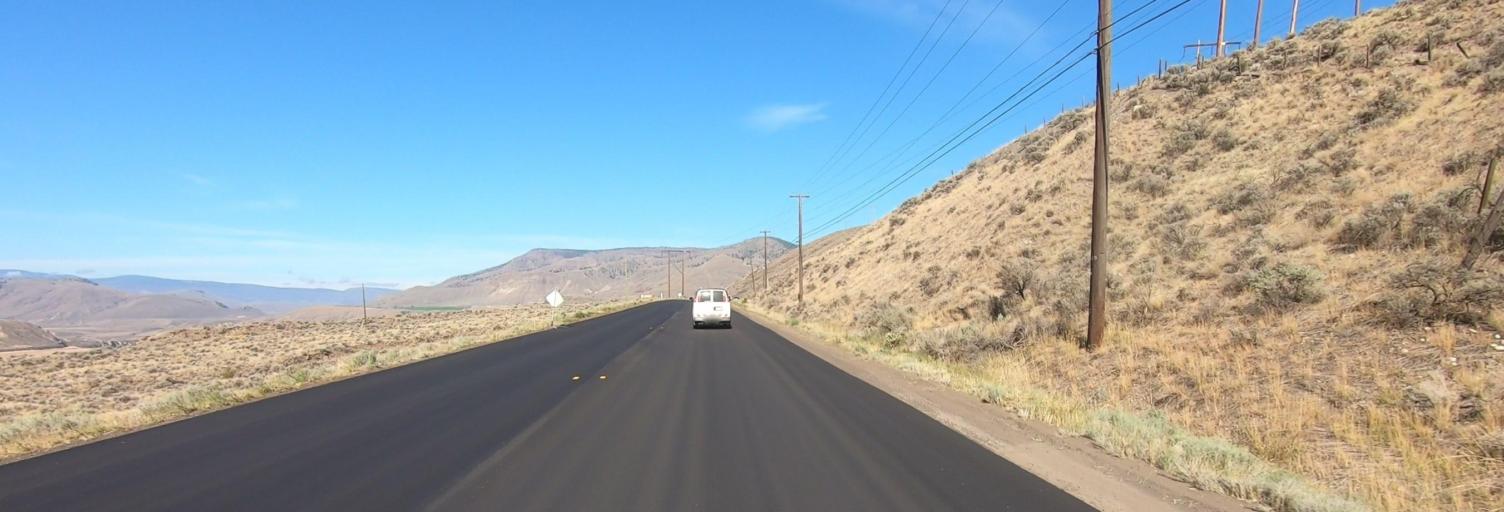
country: CA
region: British Columbia
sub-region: Thompson-Nicola Regional District
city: Ashcroft
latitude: 50.7874
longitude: -121.0702
